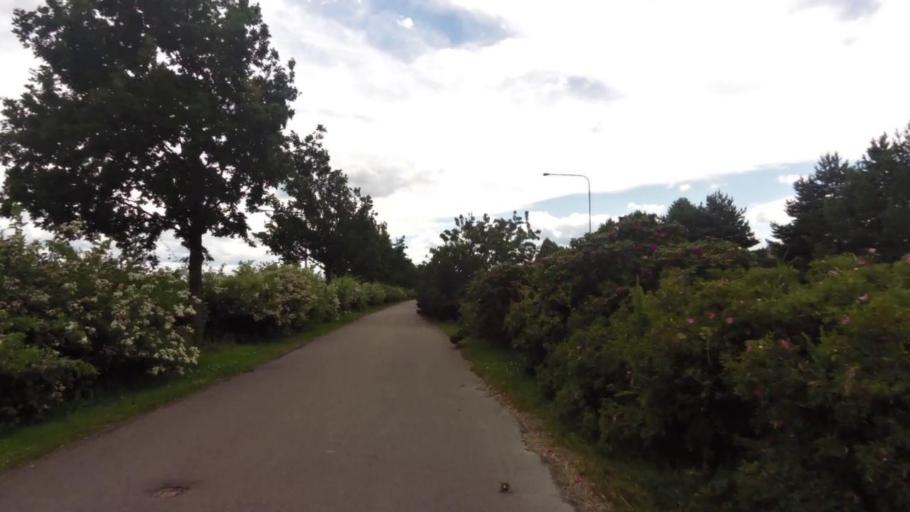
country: SE
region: OEstergoetland
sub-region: Linkopings Kommun
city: Linkoping
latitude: 58.3958
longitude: 15.5705
